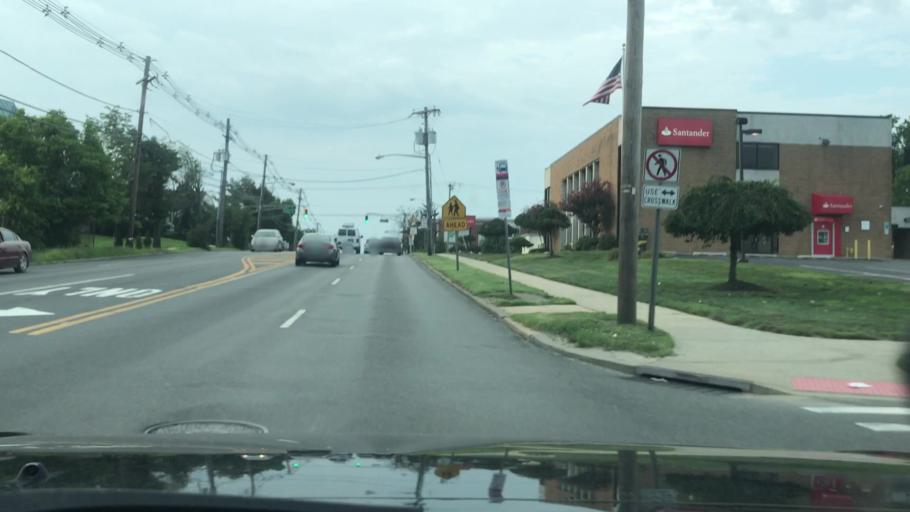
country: US
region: New Jersey
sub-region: Ocean County
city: Lakewood
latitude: 40.0949
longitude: -74.2172
